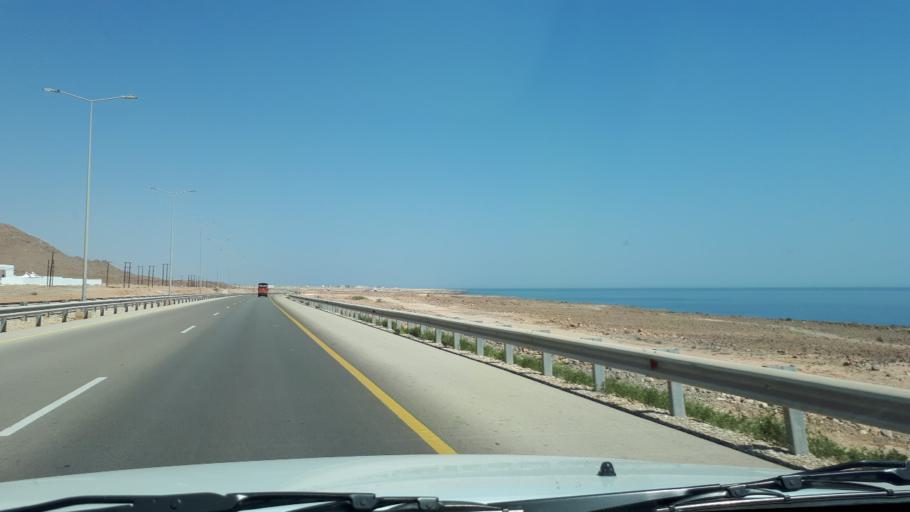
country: OM
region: Ash Sharqiyah
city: Sur
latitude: 22.7197
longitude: 59.3490
